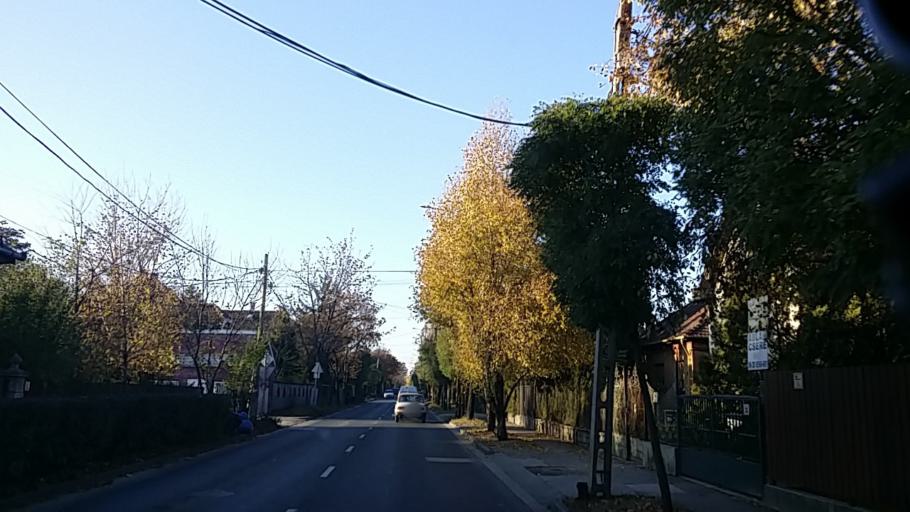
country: HU
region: Budapest
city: Budapest XVI. keruelet
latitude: 47.5123
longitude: 19.1947
